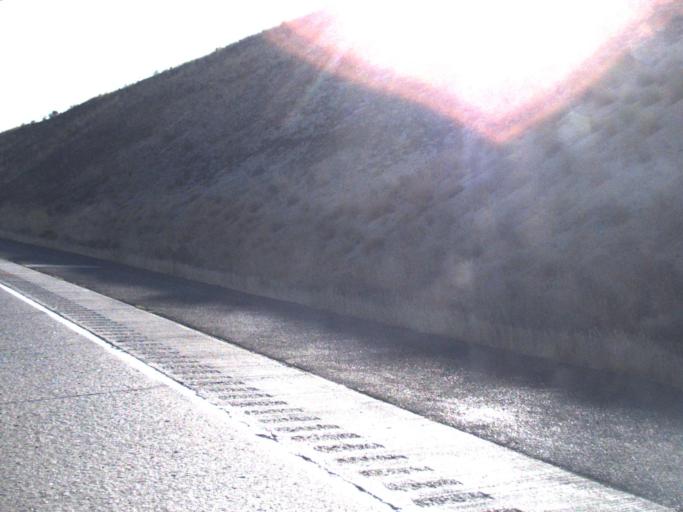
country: US
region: Washington
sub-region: Yakima County
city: Terrace Heights
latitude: 46.7257
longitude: -120.3931
